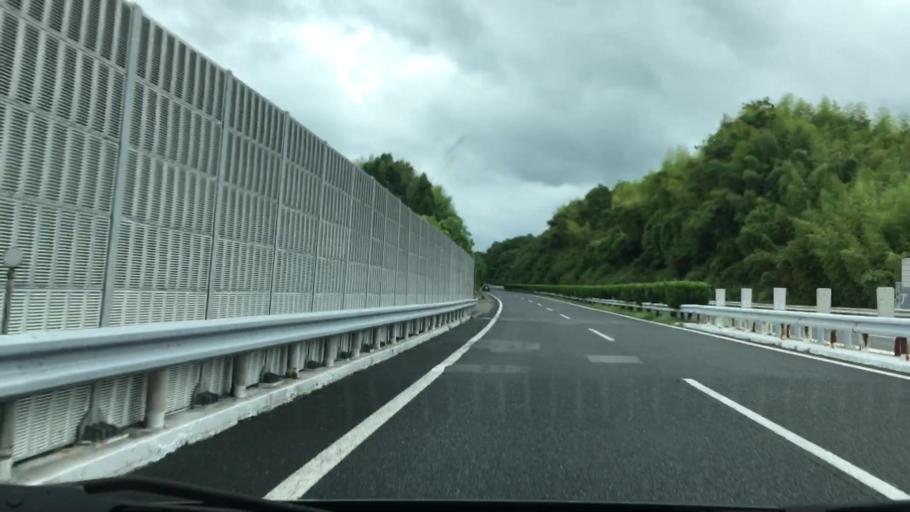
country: JP
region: Okayama
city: Tsuyama
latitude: 35.0444
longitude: 134.1144
